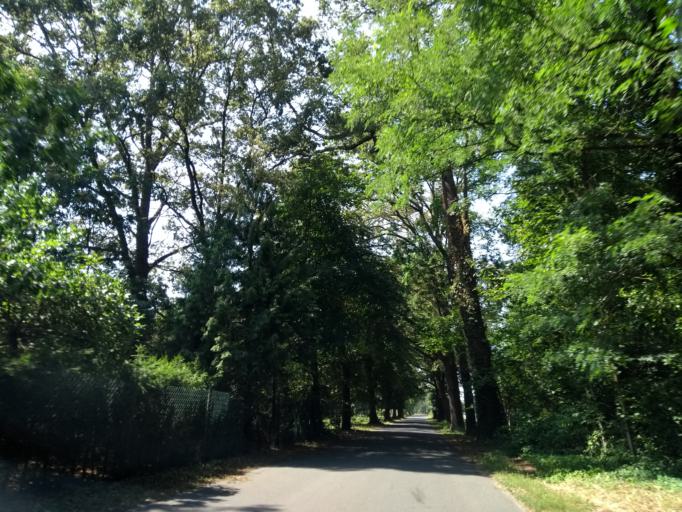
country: DE
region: Brandenburg
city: Burg
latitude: 51.8440
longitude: 14.1418
